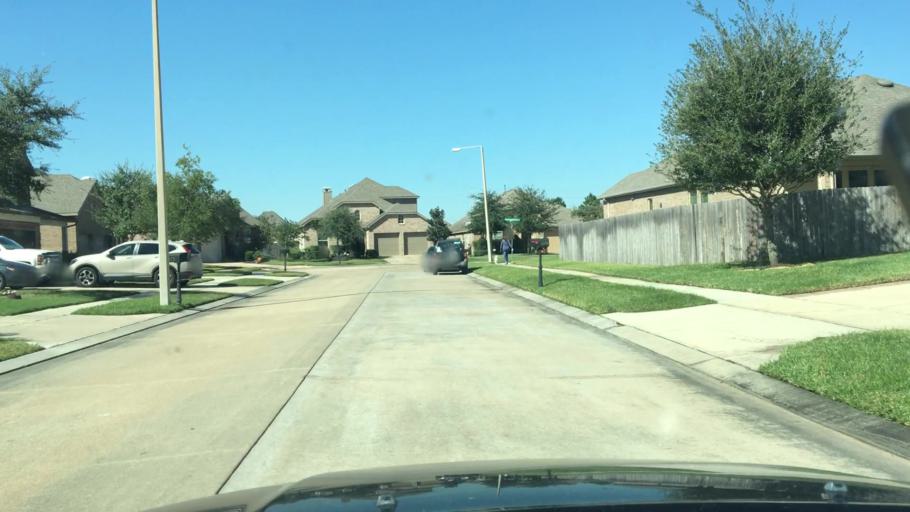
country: US
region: Texas
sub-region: Galveston County
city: Friendswood
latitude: 29.4741
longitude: -95.1659
